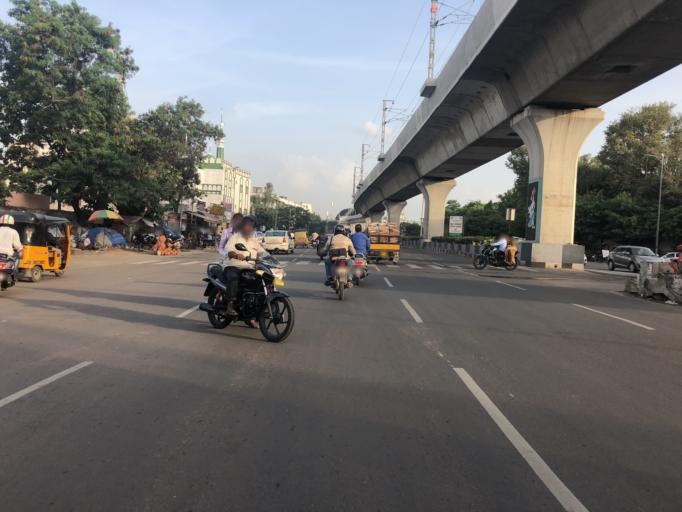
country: IN
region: Telangana
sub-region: Rangareddi
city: Kukatpalli
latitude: 17.4513
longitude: 78.4365
